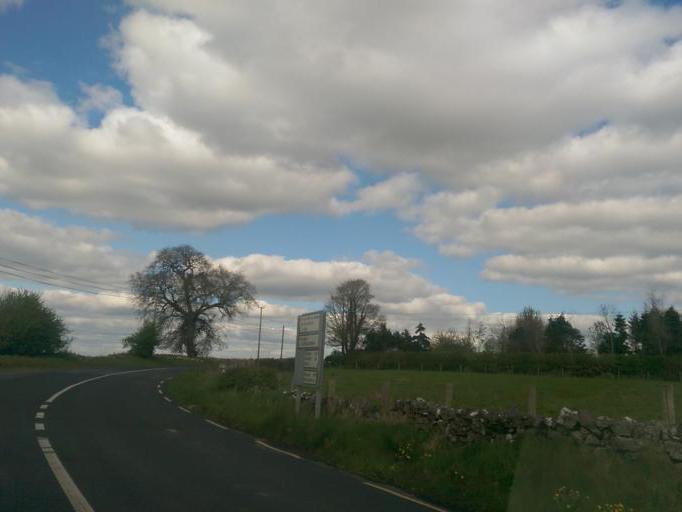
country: IE
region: Connaught
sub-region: County Galway
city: Loughrea
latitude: 53.4240
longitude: -8.5067
